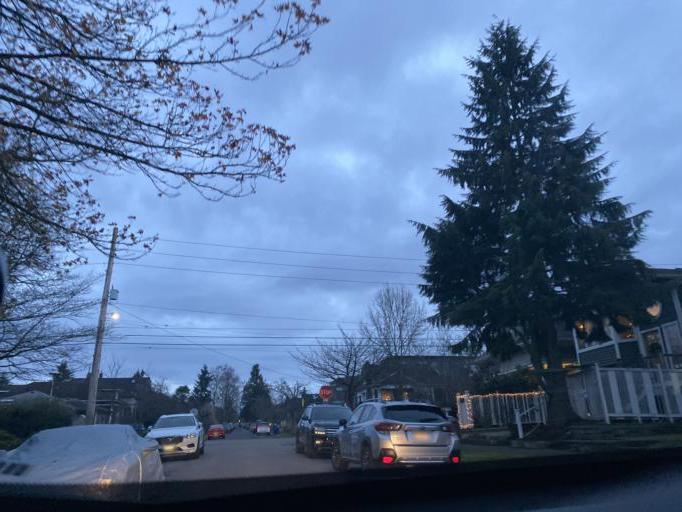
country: US
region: Washington
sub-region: King County
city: Seattle
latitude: 47.6400
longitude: -122.3636
